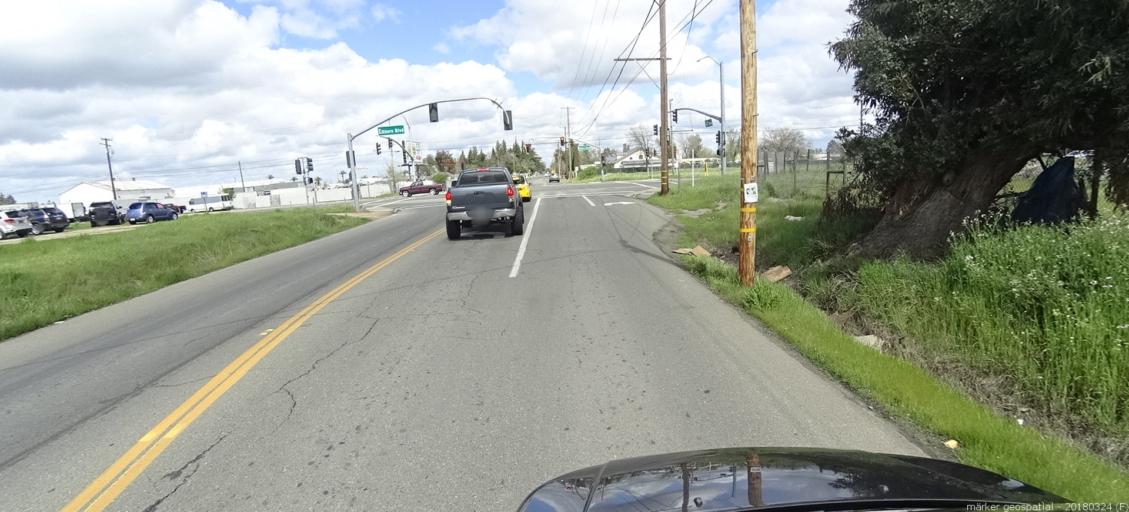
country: US
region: California
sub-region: Sacramento County
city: North Highlands
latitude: 38.6897
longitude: -121.3921
